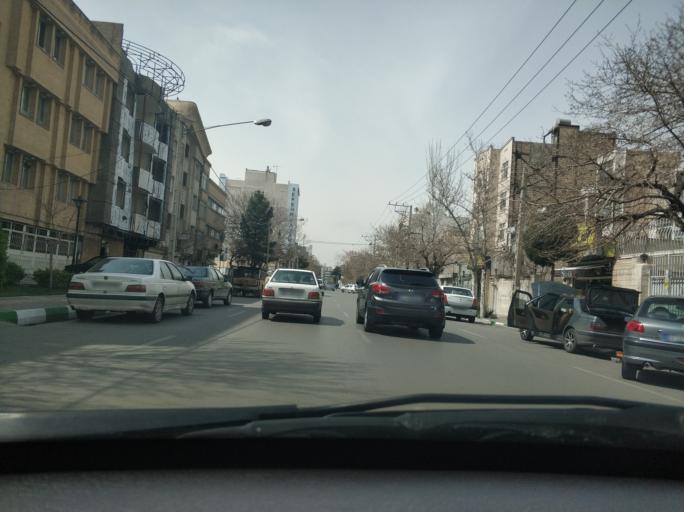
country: IR
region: Razavi Khorasan
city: Mashhad
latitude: 36.3049
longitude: 59.5687
